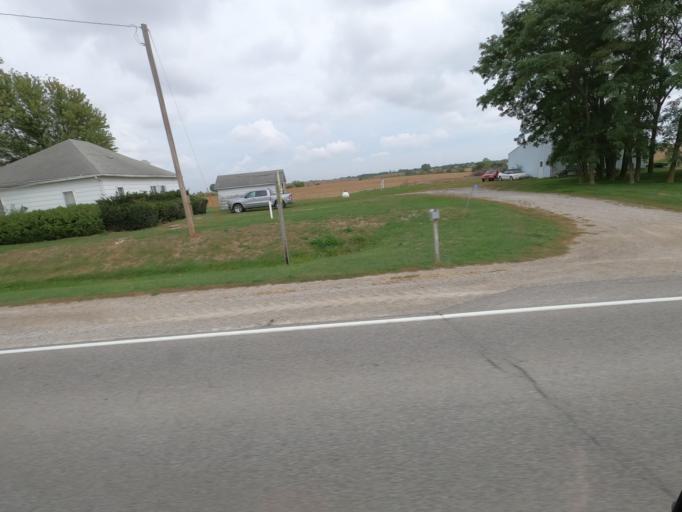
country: US
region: Iowa
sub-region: Wapello County
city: Ottumwa
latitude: 40.9586
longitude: -92.2365
